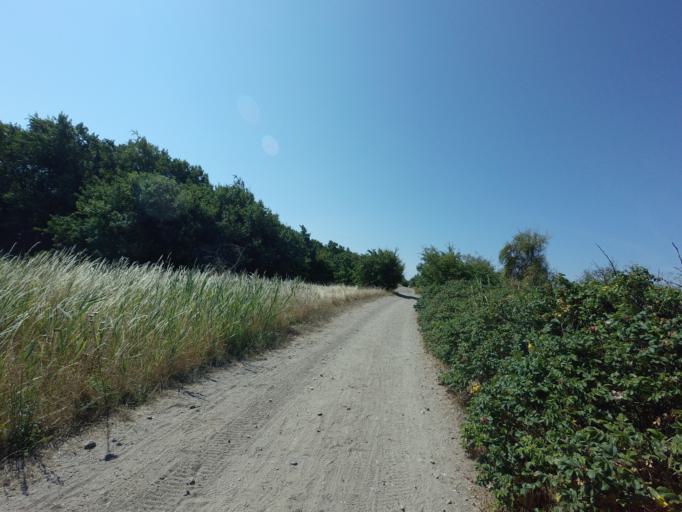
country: SE
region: Skane
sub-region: Vellinge Kommun
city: Skanor med Falsterbo
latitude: 55.4058
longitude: 12.8358
